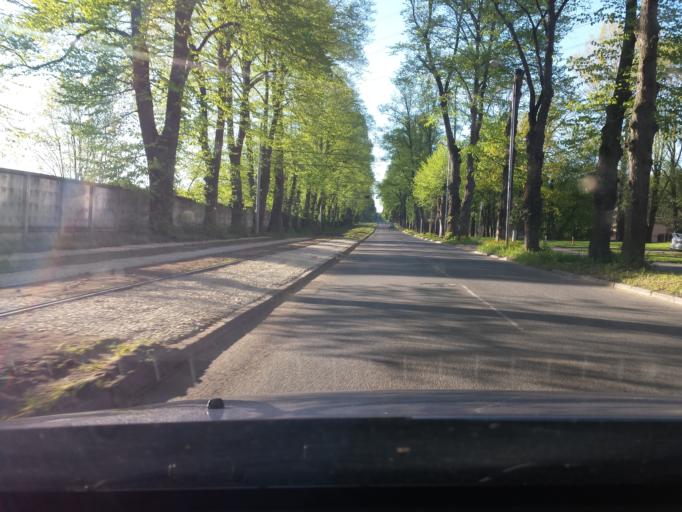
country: LV
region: Riga
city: Jaunciems
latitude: 56.9941
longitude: 24.1635
